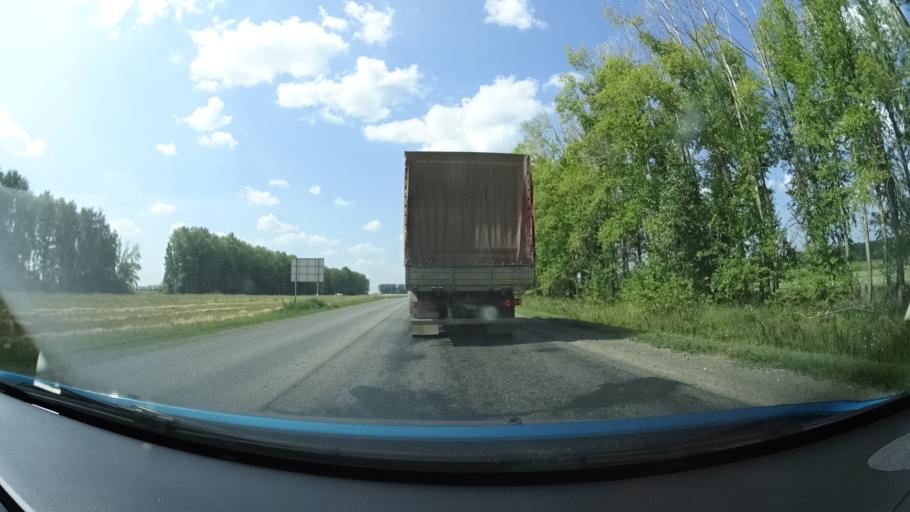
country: RU
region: Bashkortostan
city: Buzdyak
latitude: 54.6204
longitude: 54.4011
